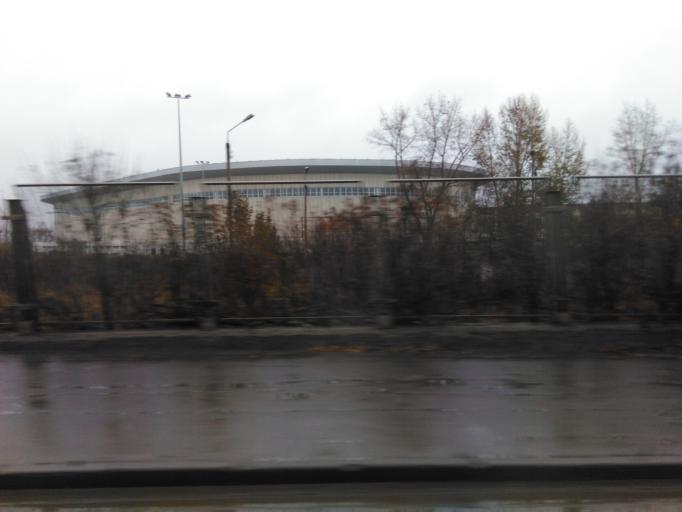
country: RU
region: Tatarstan
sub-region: Gorod Kazan'
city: Kazan
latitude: 55.7950
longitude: 49.0945
